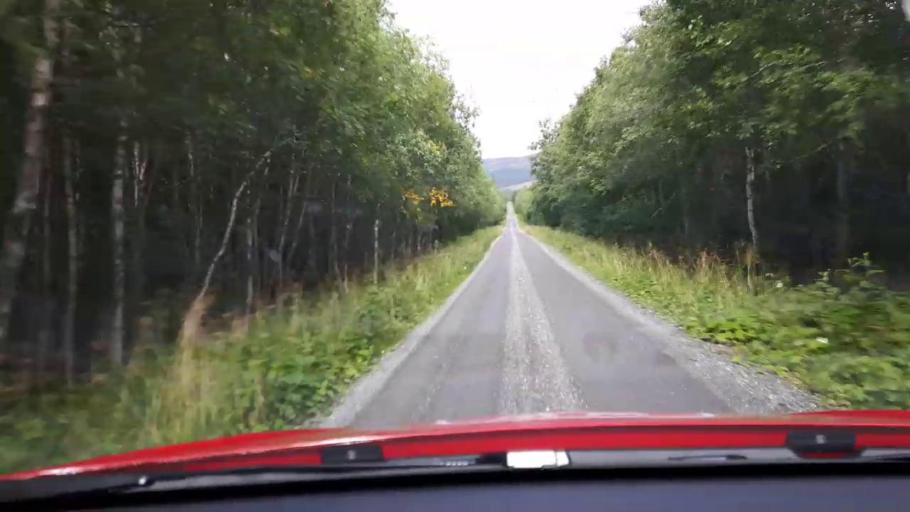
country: SE
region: Jaemtland
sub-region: Are Kommun
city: Are
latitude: 63.7911
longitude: 13.1067
